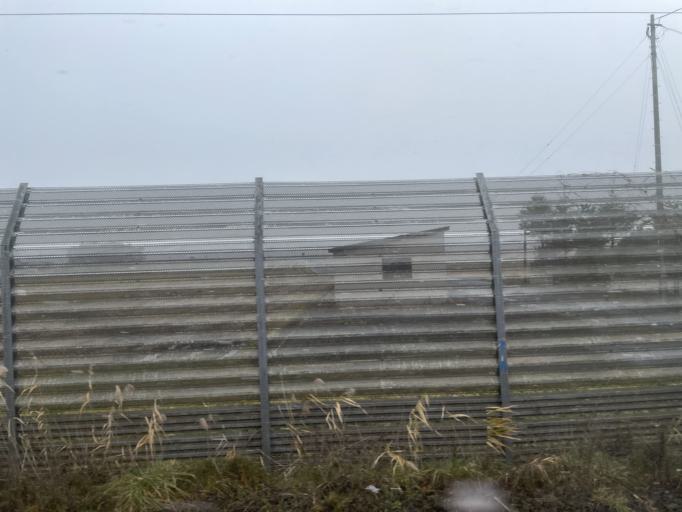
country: JP
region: Aomori
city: Aomori Shi
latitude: 40.8997
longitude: 140.6728
